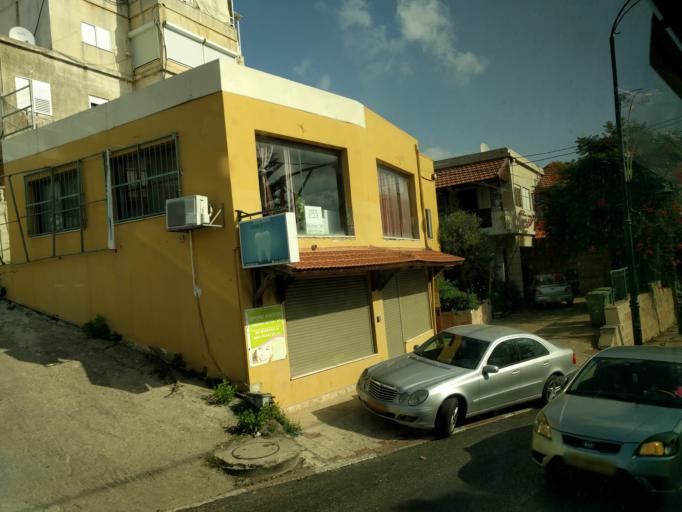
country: IL
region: Haifa
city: Daliyat el Karmil
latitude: 32.7187
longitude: 35.0649
